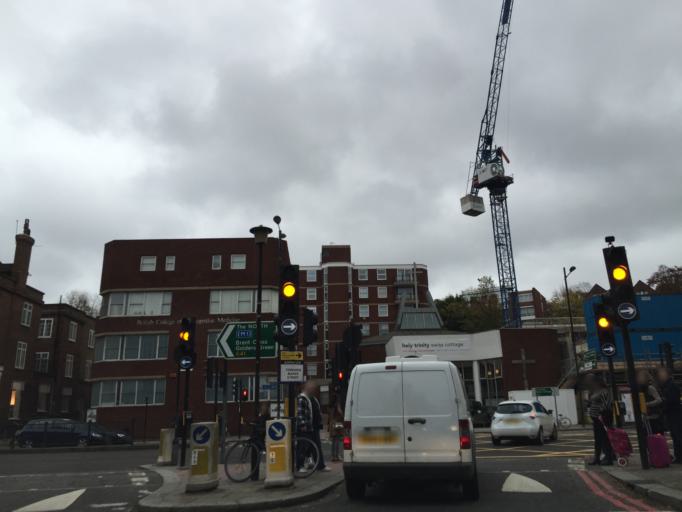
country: GB
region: England
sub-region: Greater London
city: Belsize Park
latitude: 51.5468
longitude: -0.1799
